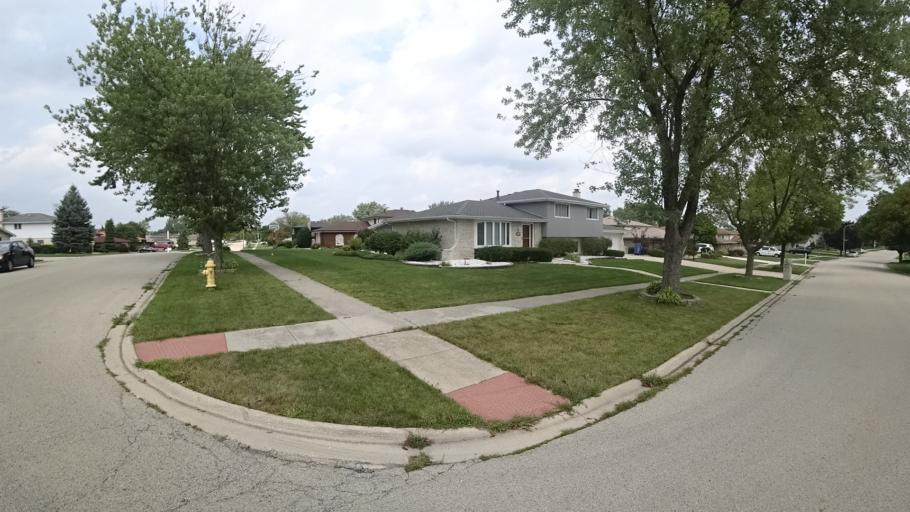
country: US
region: Illinois
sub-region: Will County
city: Goodings Grove
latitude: 41.6314
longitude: -87.9138
